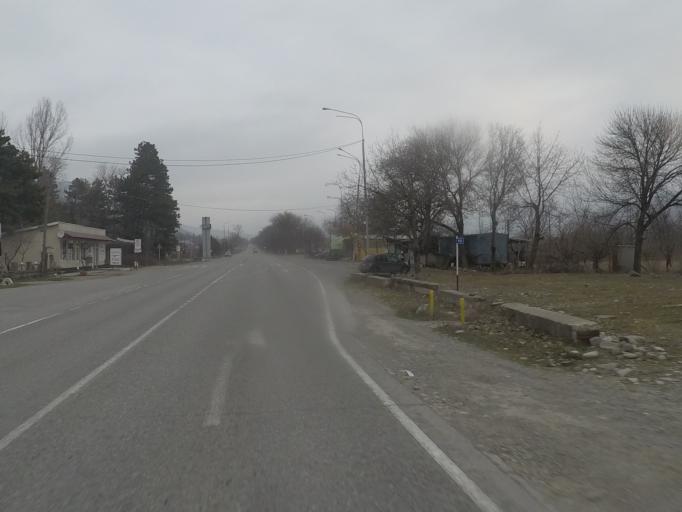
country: GE
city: Zhinvali
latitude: 42.0624
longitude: 44.7457
